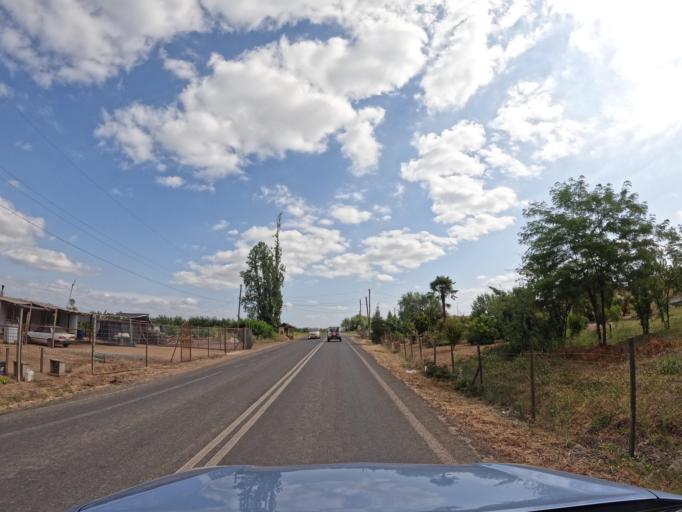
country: CL
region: Maule
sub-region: Provincia de Curico
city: Molina
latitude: -35.2021
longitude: -71.2973
